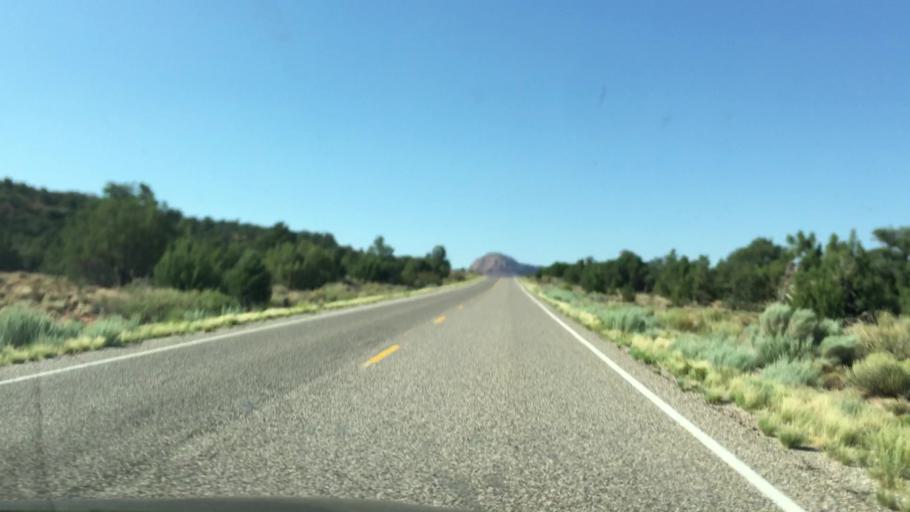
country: US
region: Arizona
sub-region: Coconino County
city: Fredonia
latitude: 36.8696
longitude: -112.7377
